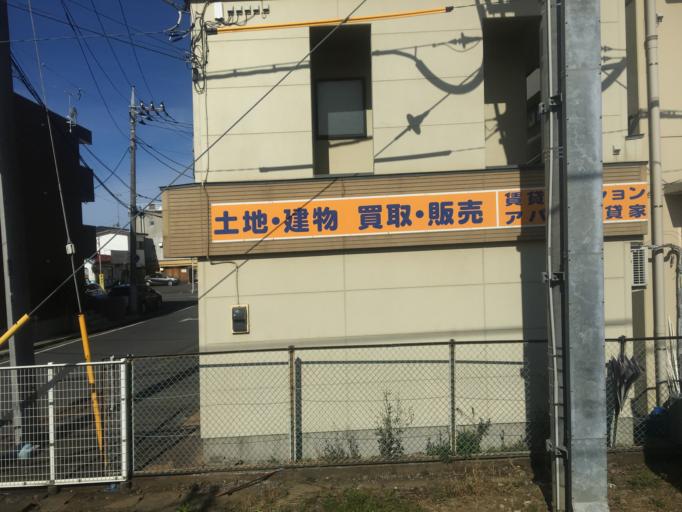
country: JP
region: Saitama
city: Sakado
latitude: 35.9719
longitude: 139.3964
